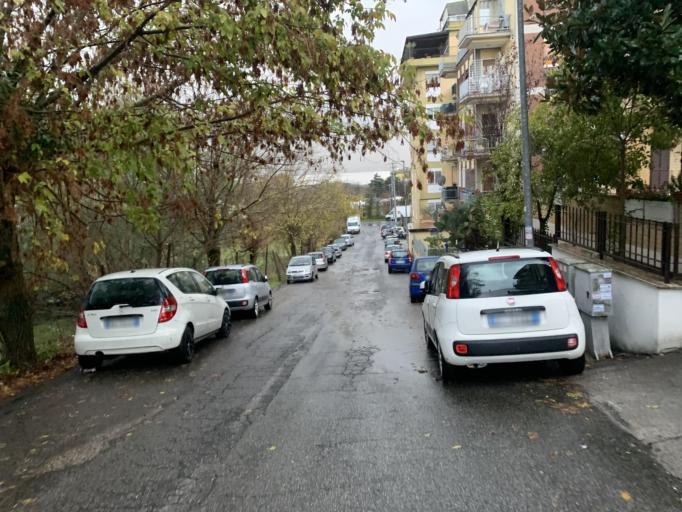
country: IT
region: Latium
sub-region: Citta metropolitana di Roma Capitale
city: Setteville
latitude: 41.9436
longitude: 12.6551
